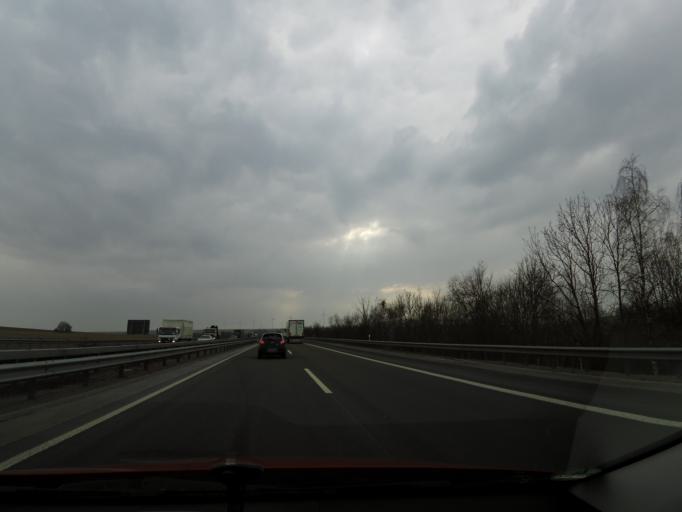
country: DE
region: Rheinland-Pfalz
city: Dintesheim
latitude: 49.7286
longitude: 8.1366
